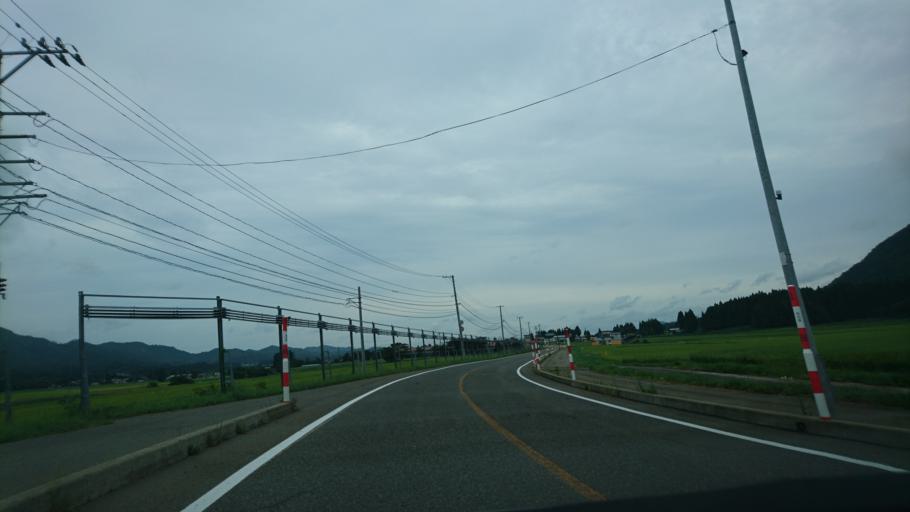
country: JP
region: Akita
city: Yuzawa
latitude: 39.1201
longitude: 140.5785
